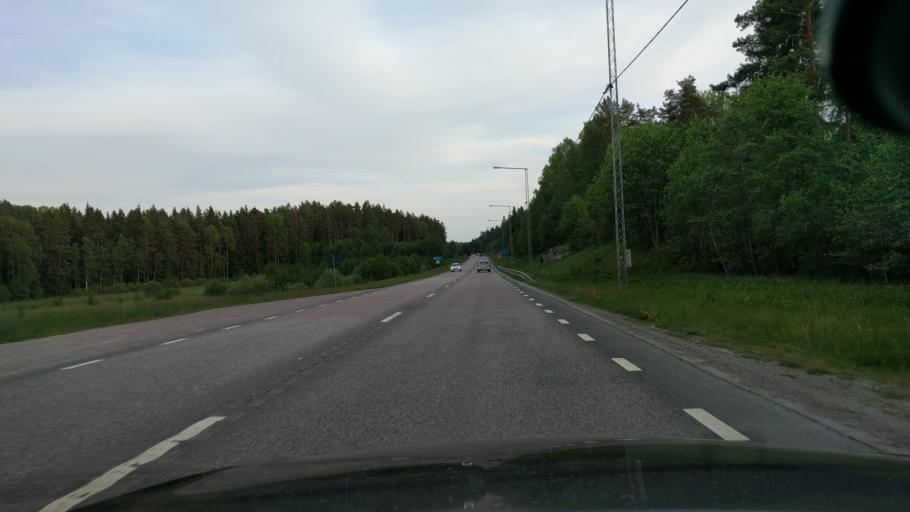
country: SE
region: Stockholm
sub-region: Vallentuna Kommun
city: Vallentuna
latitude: 59.5051
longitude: 18.0992
